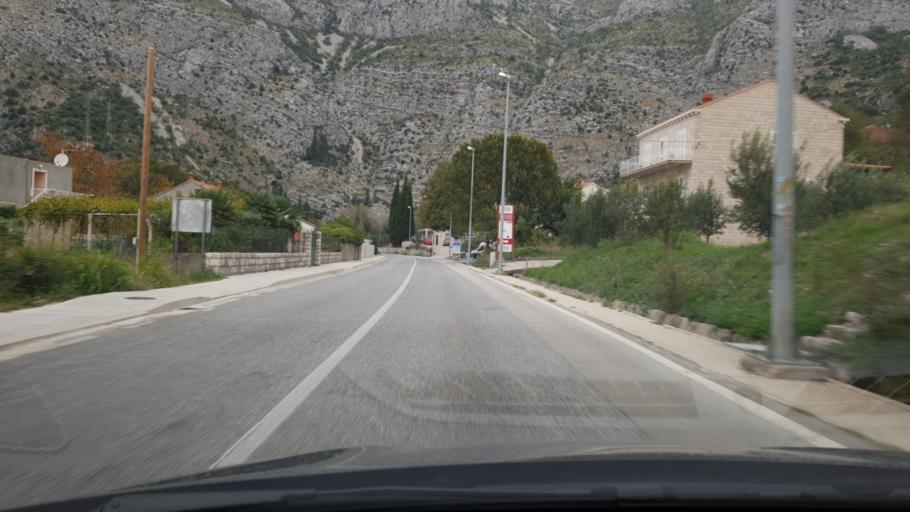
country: HR
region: Dubrovacko-Neretvanska
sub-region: Grad Dubrovnik
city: Mokosica
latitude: 42.6712
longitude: 18.1356
